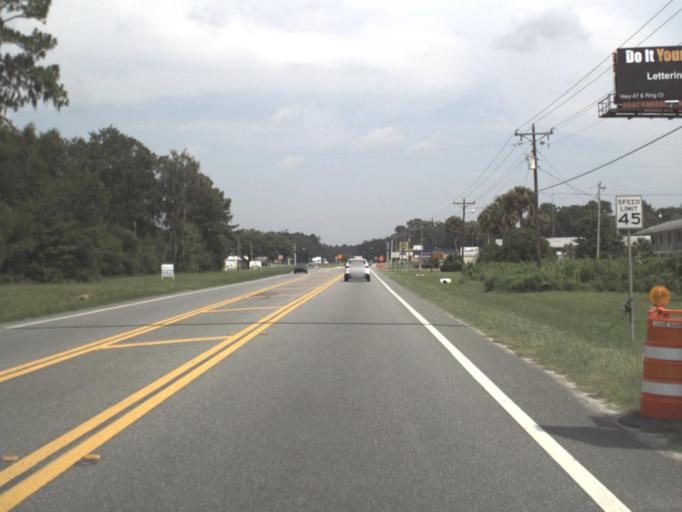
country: US
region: Florida
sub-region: Columbia County
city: Lake City
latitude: 30.1420
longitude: -82.6353
